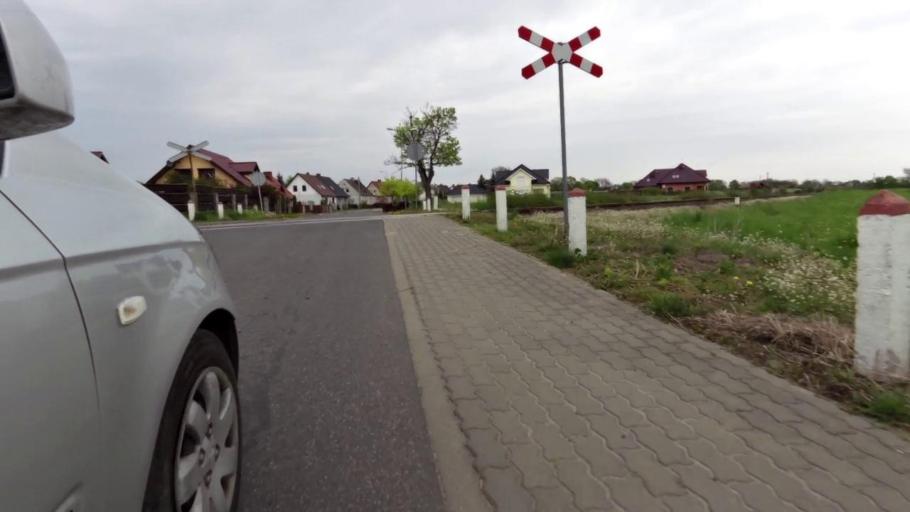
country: PL
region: West Pomeranian Voivodeship
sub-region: Powiat walecki
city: Walcz
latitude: 53.2720
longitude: 16.4341
